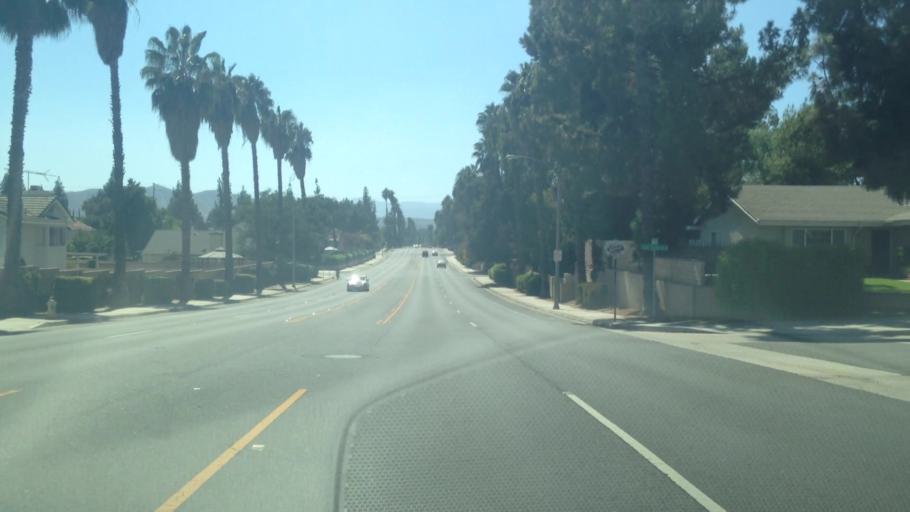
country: US
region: California
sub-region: Riverside County
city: Riverside
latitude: 33.9117
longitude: -117.4299
